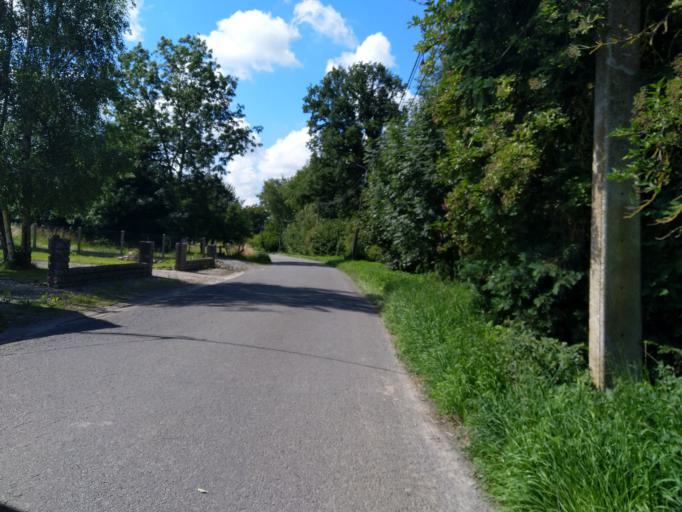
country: BE
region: Wallonia
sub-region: Province du Hainaut
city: Beloeil
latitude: 50.6007
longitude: 3.6837
